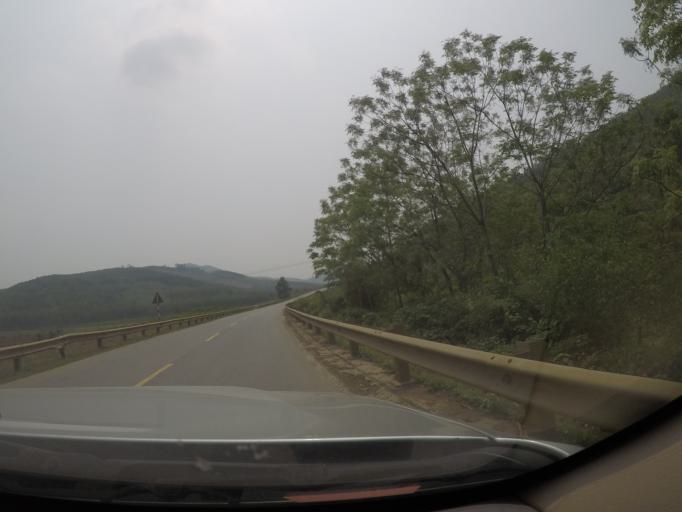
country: VN
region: Thanh Hoa
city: Thi Tran Cam Thuy
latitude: 20.1808
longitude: 105.4785
